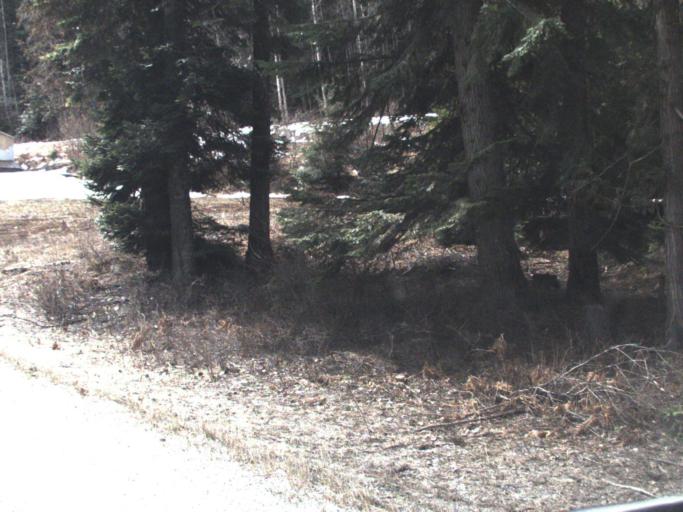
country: US
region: Washington
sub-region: Pend Oreille County
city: Newport
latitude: 48.5063
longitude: -117.2757
